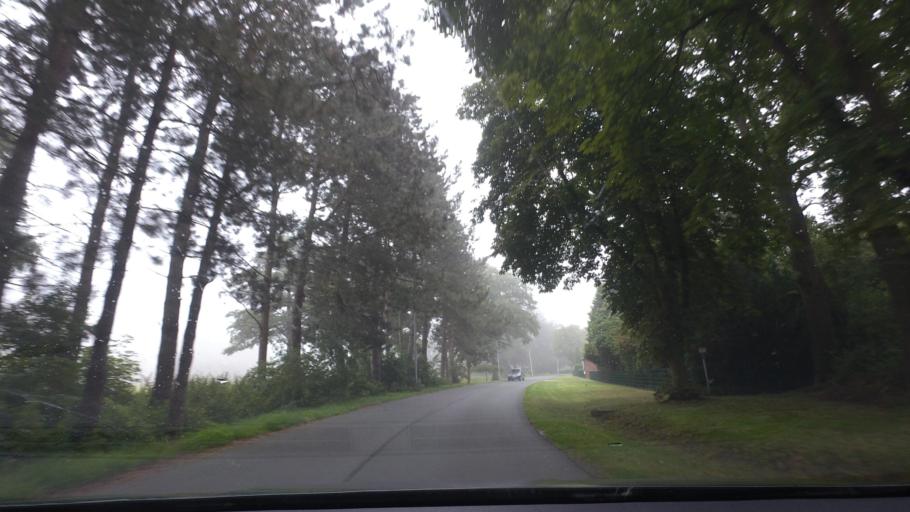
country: DE
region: Lower Saxony
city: Hatten
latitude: 53.1186
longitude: 8.3497
